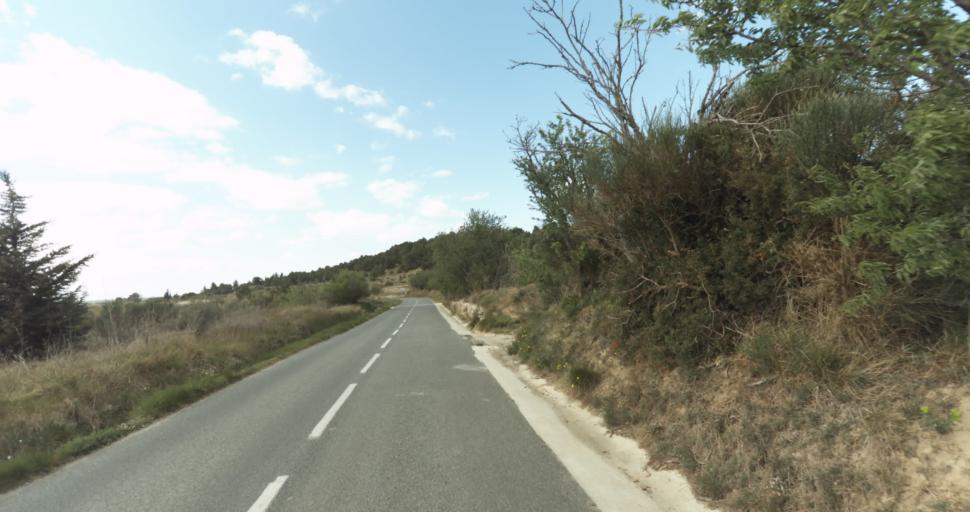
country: FR
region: Languedoc-Roussillon
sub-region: Departement de l'Aude
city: Leucate
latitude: 42.9259
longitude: 3.0140
